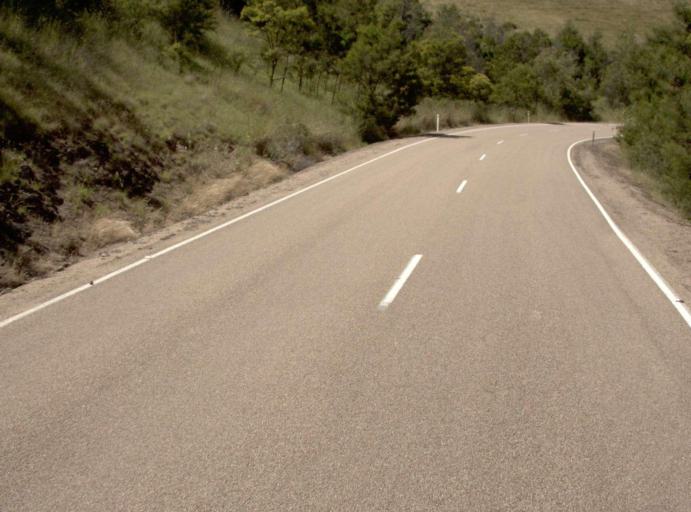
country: AU
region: Victoria
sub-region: East Gippsland
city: Lakes Entrance
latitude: -37.4881
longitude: 148.1869
